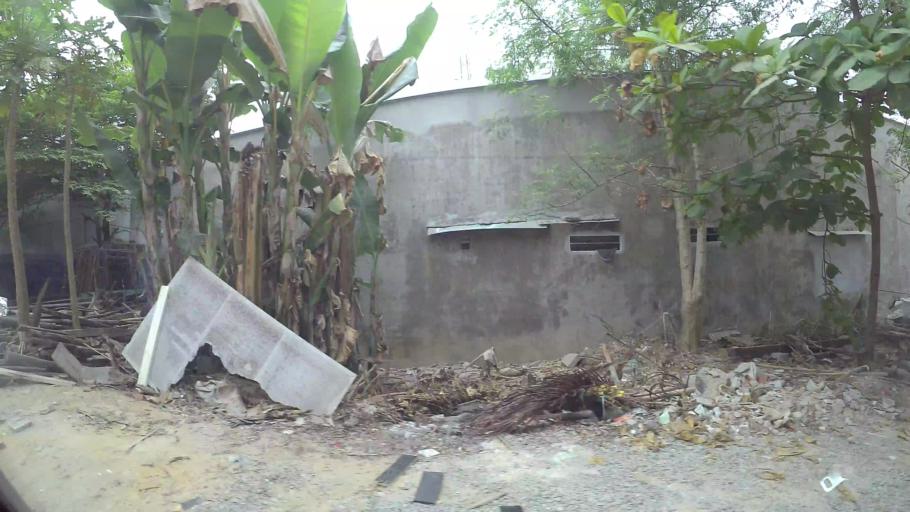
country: VN
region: Da Nang
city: Lien Chieu
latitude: 16.0728
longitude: 108.1673
